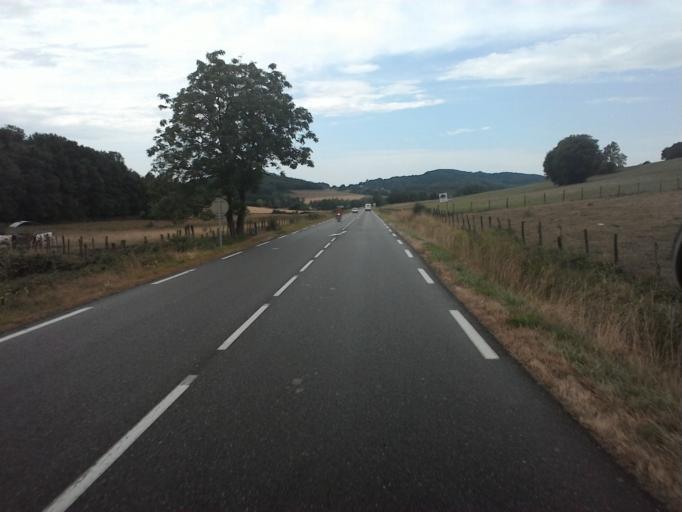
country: FR
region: Franche-Comte
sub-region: Departement du Jura
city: Poligny
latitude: 46.8223
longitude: 5.5945
